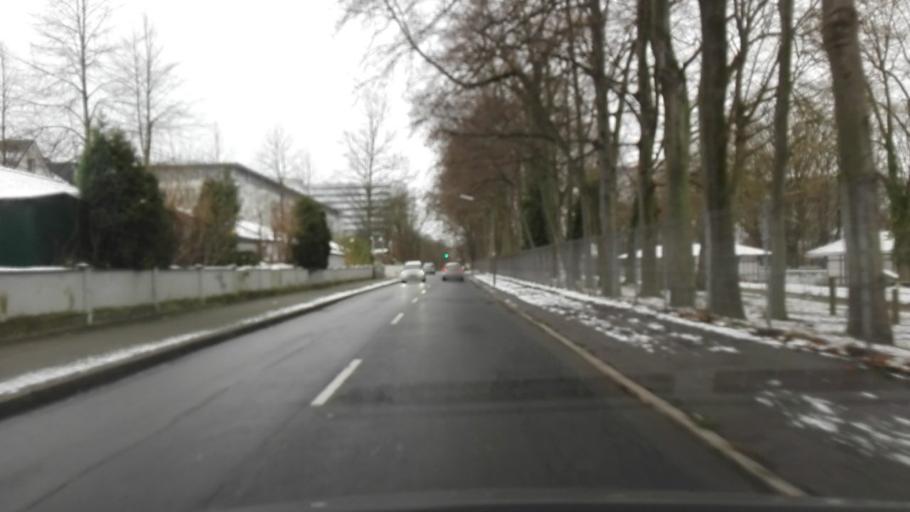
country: DE
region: North Rhine-Westphalia
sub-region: Regierungsbezirk Arnsberg
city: Dortmund
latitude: 51.5119
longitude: 7.5268
